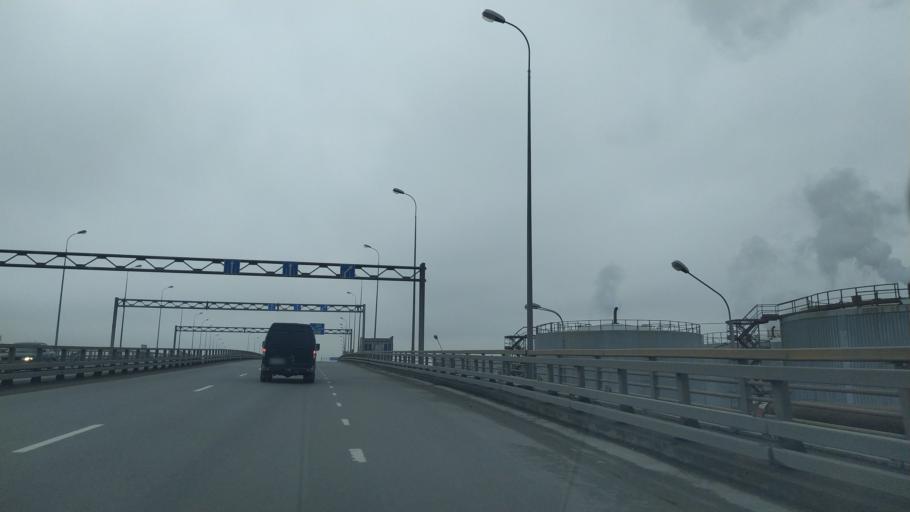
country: RU
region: St.-Petersburg
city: Dachnoye
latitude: 59.8324
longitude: 30.2961
